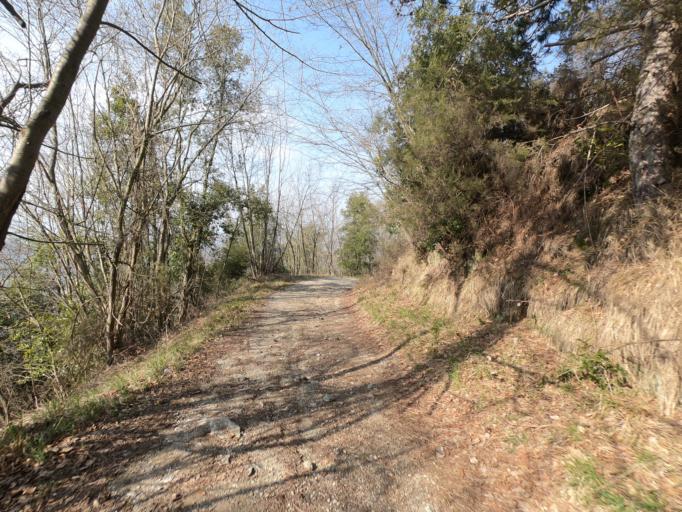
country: IT
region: Liguria
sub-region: Provincia di Savona
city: Castelvecchio di Rocca Barbena
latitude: 44.1263
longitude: 8.1411
